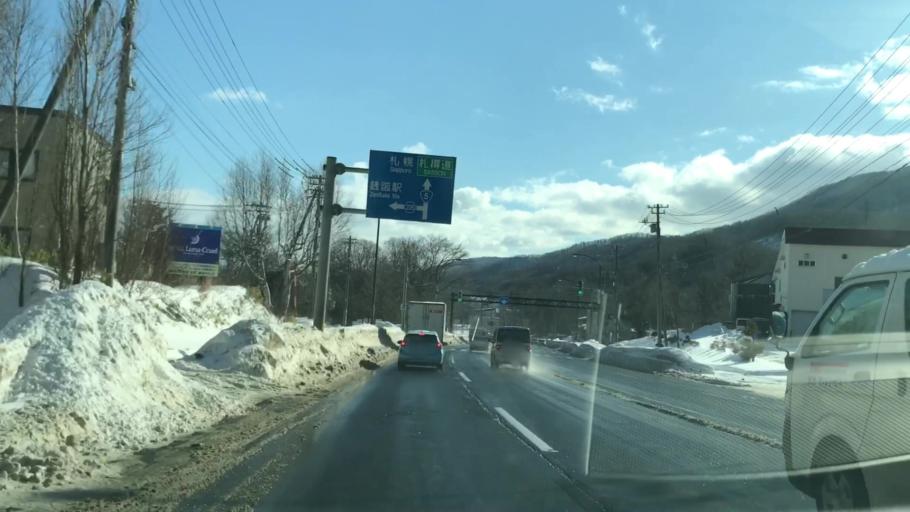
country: JP
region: Hokkaido
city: Otaru
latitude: 43.1424
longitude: 141.1493
